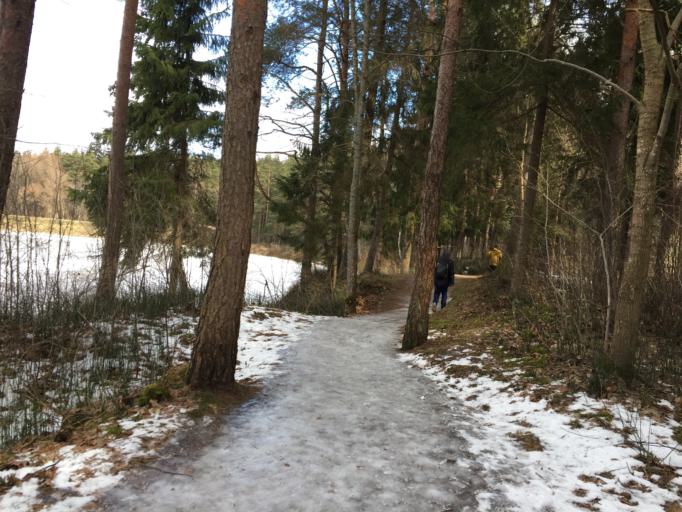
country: LV
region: Valmieras Rajons
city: Valmiera
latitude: 57.5341
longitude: 25.4351
